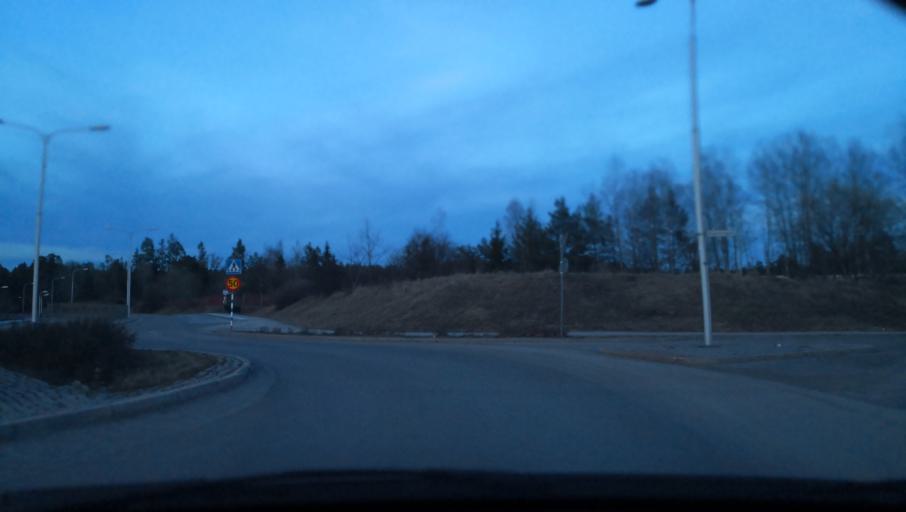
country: SE
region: Stockholm
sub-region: Varmdo Kommun
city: Gustavsberg
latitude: 59.3126
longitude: 18.3892
